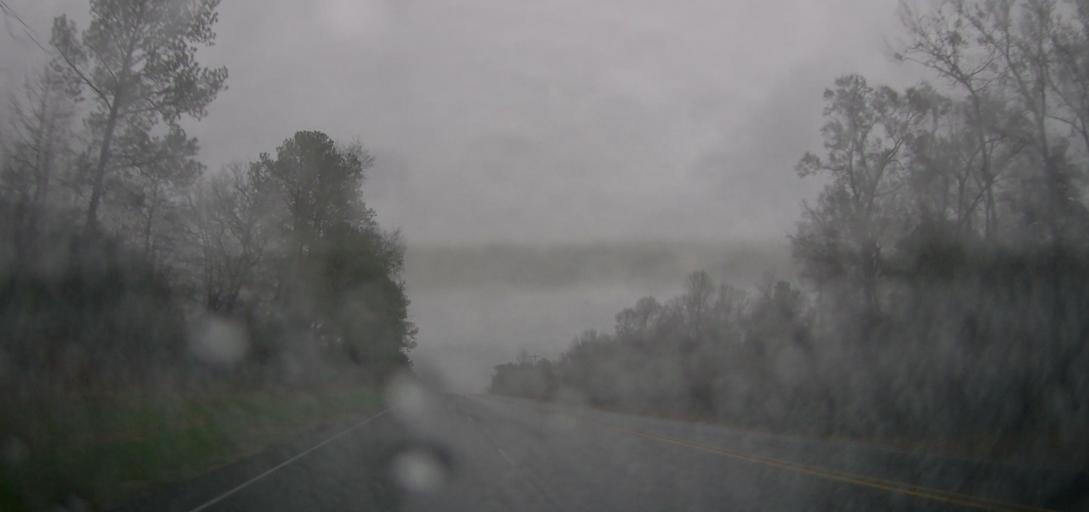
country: US
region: Alabama
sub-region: Autauga County
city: Pine Level
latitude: 32.5814
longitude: -86.6910
